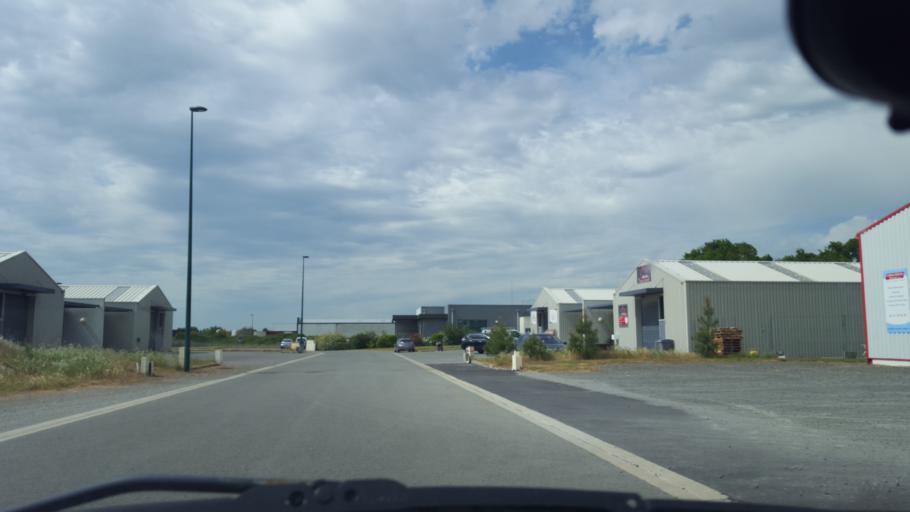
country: FR
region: Pays de la Loire
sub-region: Departement de la Loire-Atlantique
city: Machecoul
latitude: 46.9786
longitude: -1.7993
